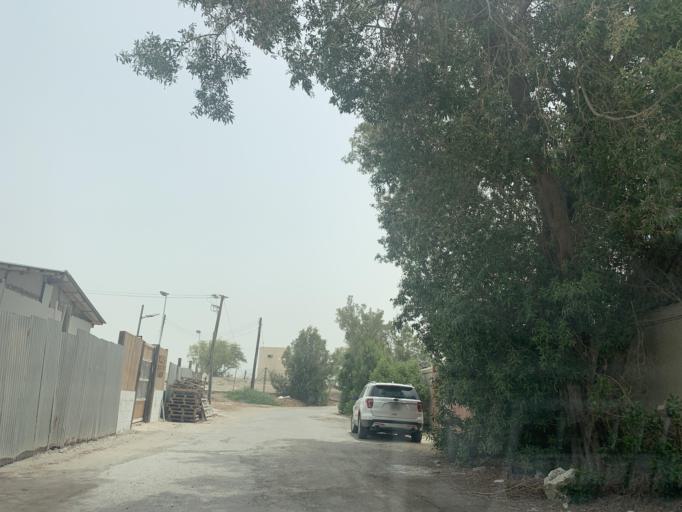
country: BH
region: Manama
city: Jidd Hafs
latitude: 26.2315
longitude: 50.5183
